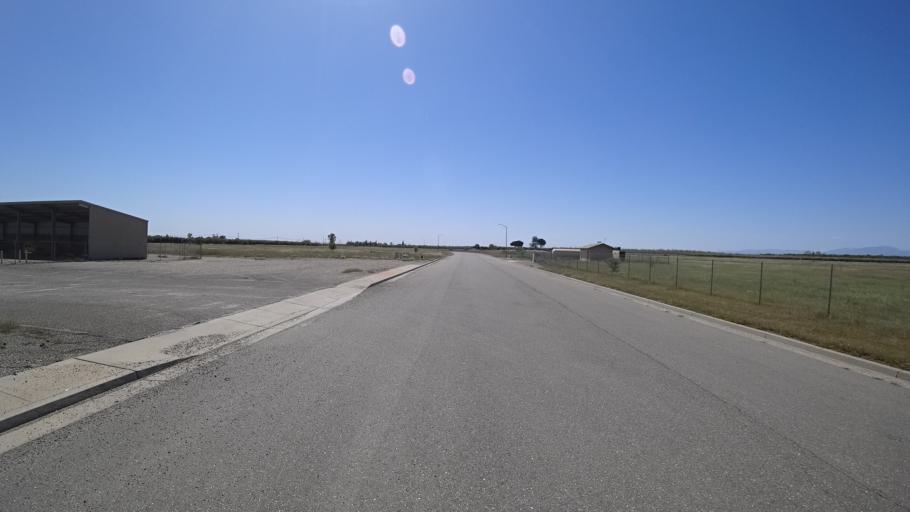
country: US
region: California
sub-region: Glenn County
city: Orland
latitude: 39.7170
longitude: -122.1432
